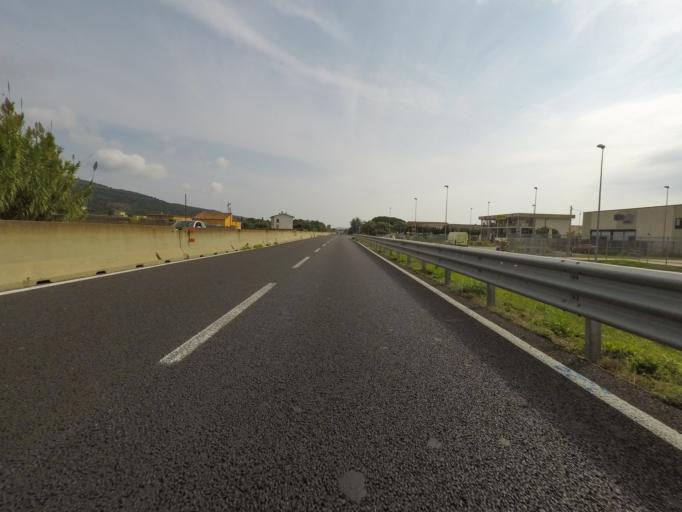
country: IT
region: Tuscany
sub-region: Provincia di Grosseto
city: Orbetello Scalo
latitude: 42.4669
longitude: 11.2399
